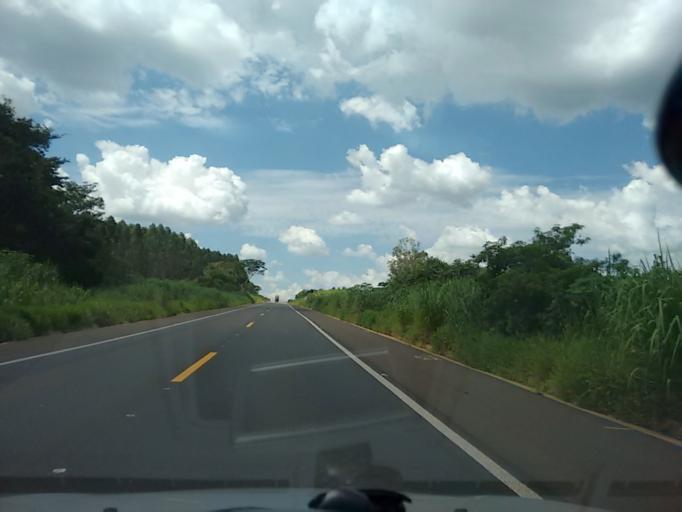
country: BR
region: Sao Paulo
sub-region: Osvaldo Cruz
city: Osvaldo Cruz
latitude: -21.8391
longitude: -50.8264
